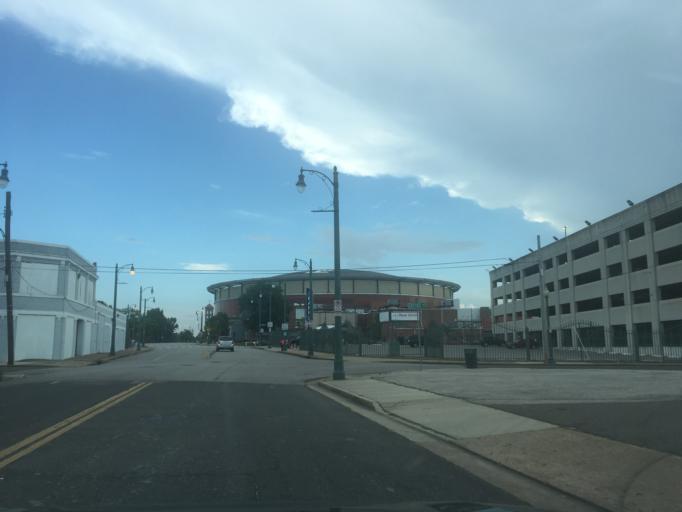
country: US
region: Tennessee
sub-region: Shelby County
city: Memphis
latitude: 35.1411
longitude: -90.0493
